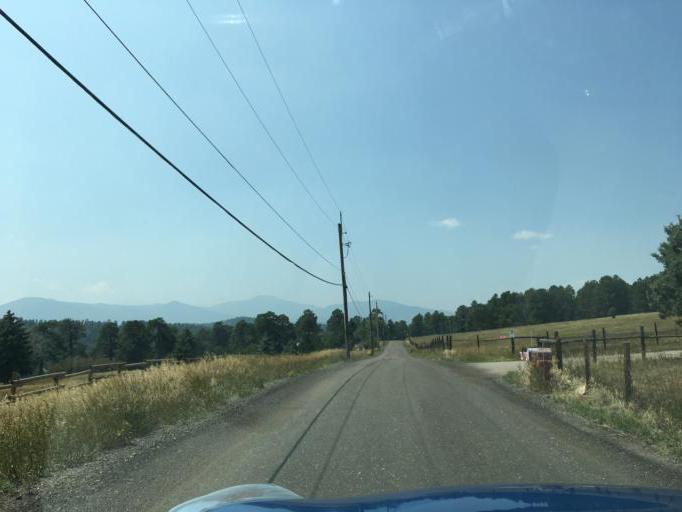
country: US
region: Colorado
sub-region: Jefferson County
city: Genesee
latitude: 39.7172
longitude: -105.2955
